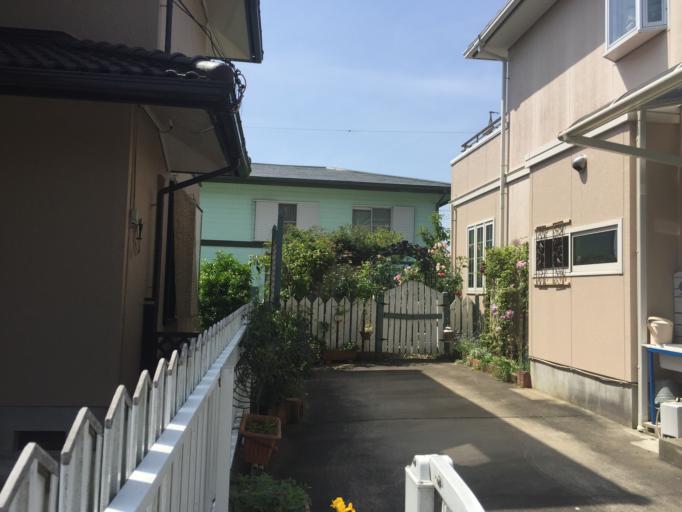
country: JP
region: Shizuoka
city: Kakegawa
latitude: 34.7818
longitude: 138.0236
